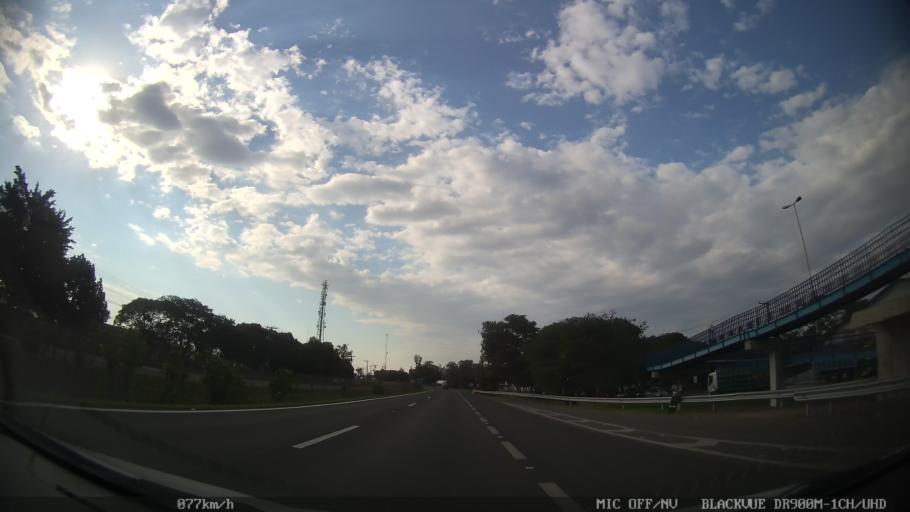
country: BR
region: Sao Paulo
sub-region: Paulinia
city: Paulinia
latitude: -22.7185
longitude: -47.1428
